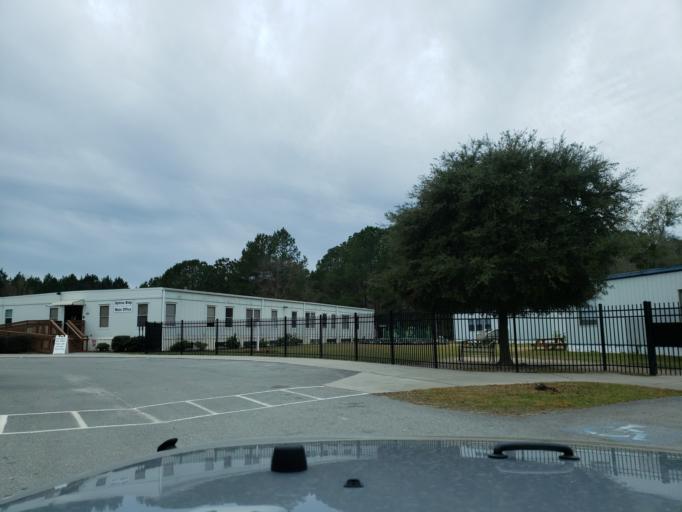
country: US
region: Georgia
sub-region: Chatham County
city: Georgetown
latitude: 32.0307
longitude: -81.1815
